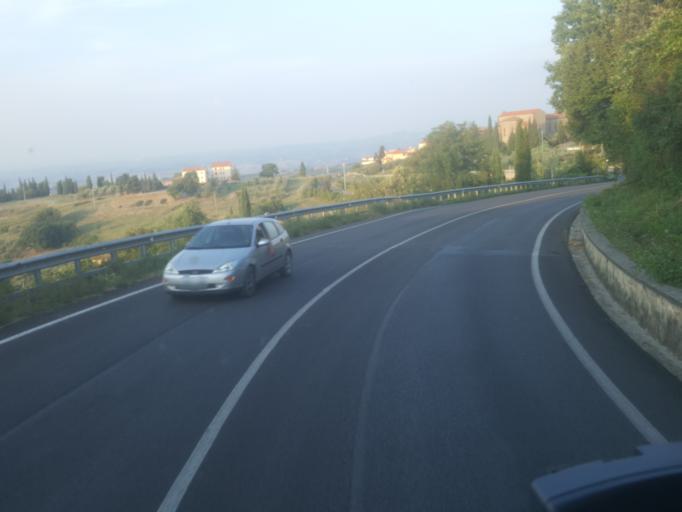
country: IT
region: Tuscany
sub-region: Province of Florence
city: Gambassi Terme
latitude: 43.5398
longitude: 10.9497
